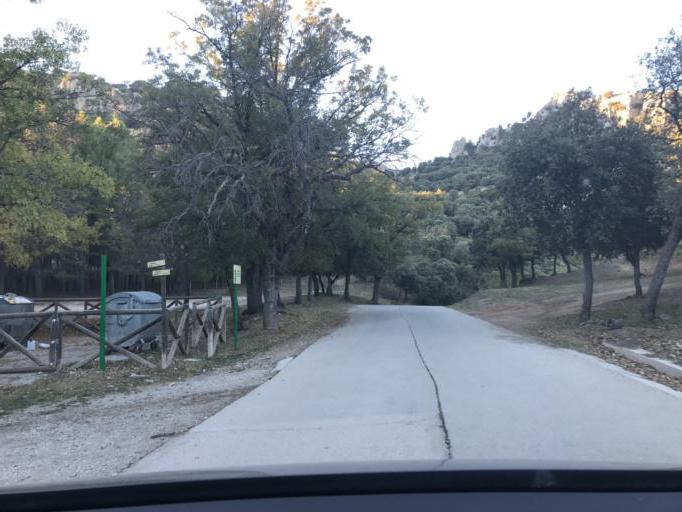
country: ES
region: Andalusia
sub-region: Provincia de Granada
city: Beas de Granada
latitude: 37.3093
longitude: -3.4643
